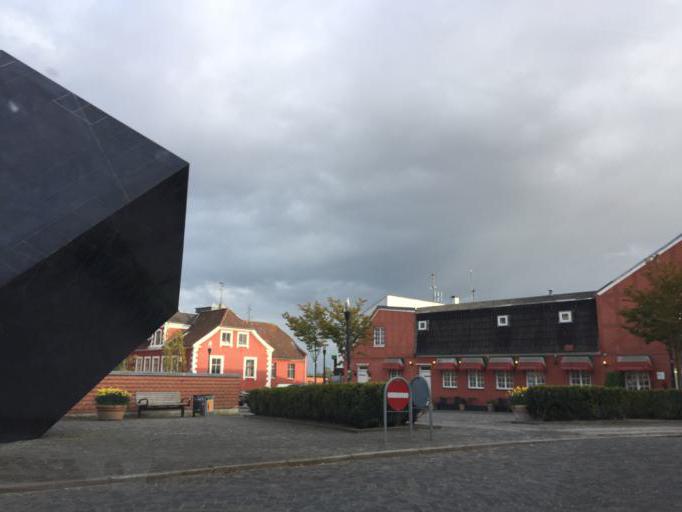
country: DK
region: South Denmark
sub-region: Svendborg Kommune
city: Svendborg
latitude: 55.0631
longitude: 10.6123
